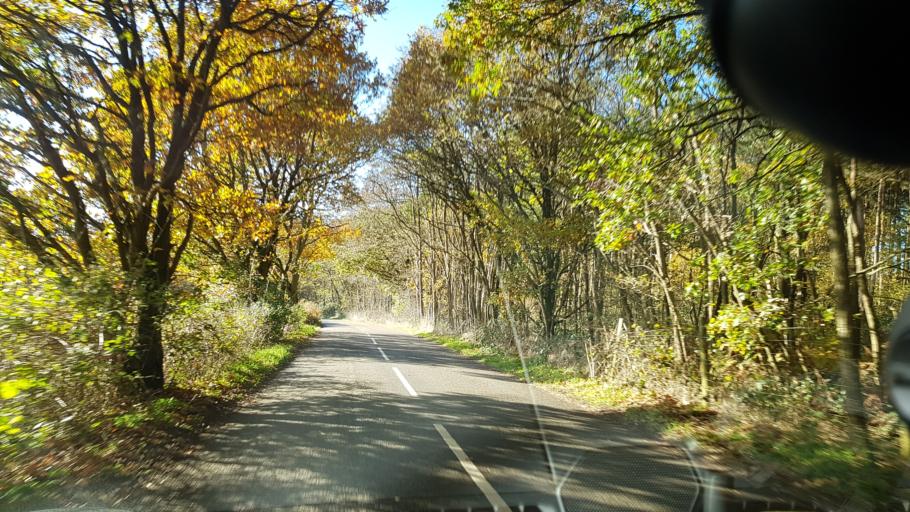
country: GB
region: England
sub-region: Surrey
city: Elstead
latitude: 51.2090
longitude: -0.6801
